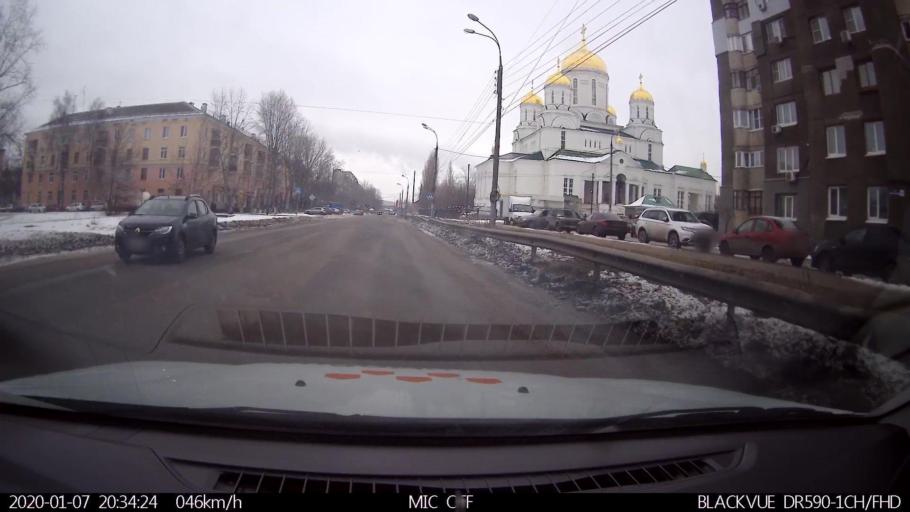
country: RU
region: Nizjnij Novgorod
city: Gorbatovka
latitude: 56.2636
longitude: 43.8785
